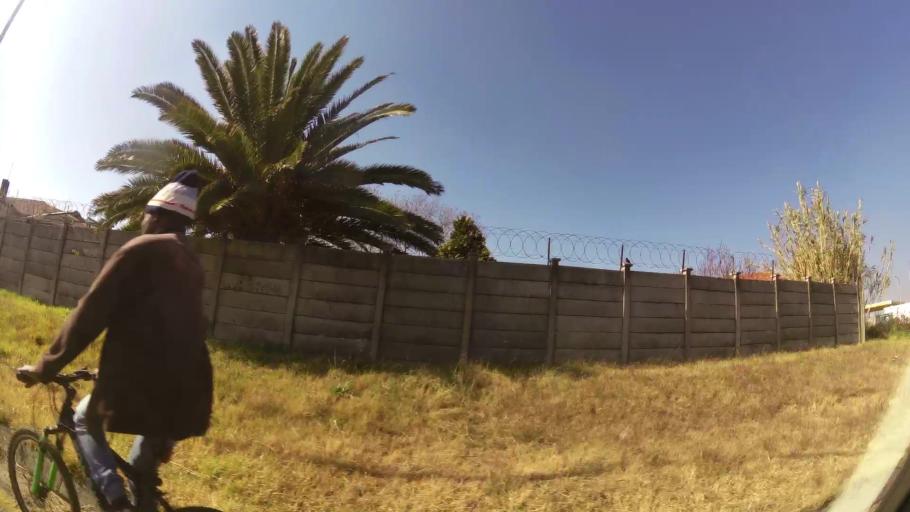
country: ZA
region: Gauteng
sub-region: City of Johannesburg Metropolitan Municipality
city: Johannesburg
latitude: -26.2603
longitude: 28.0302
